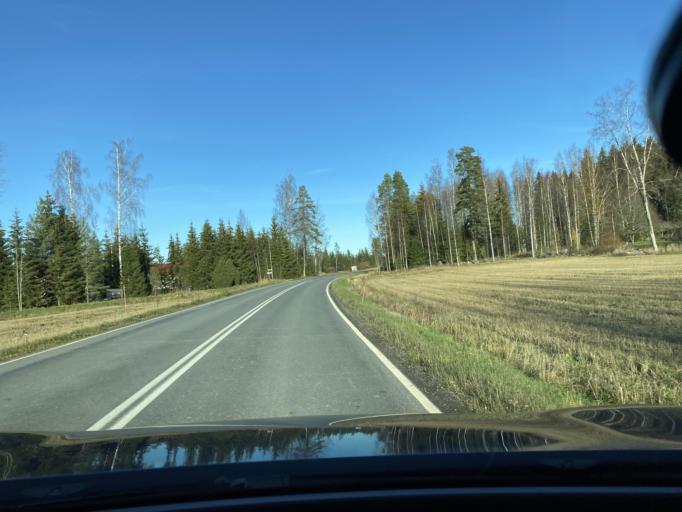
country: FI
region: Haeme
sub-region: Forssa
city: Tammela
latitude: 60.8471
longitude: 23.8379
